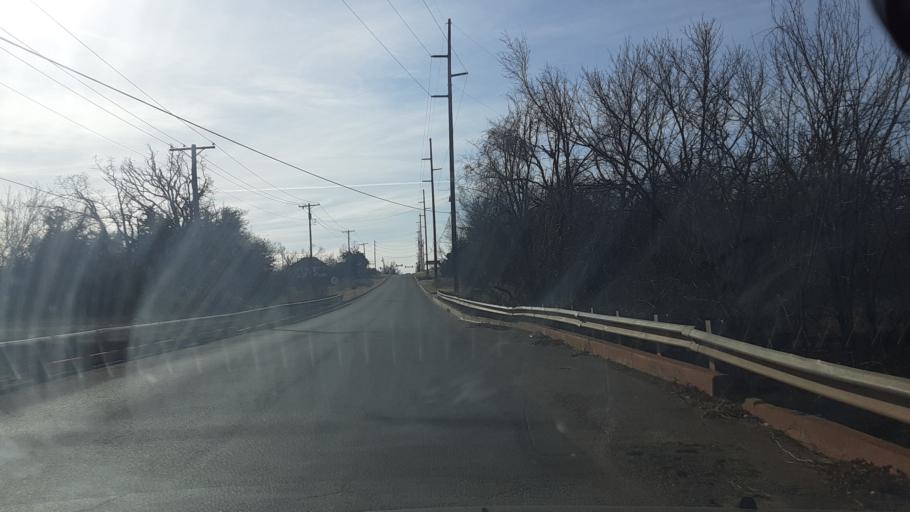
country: US
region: Oklahoma
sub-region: Logan County
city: Guthrie
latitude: 35.8838
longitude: -97.4075
